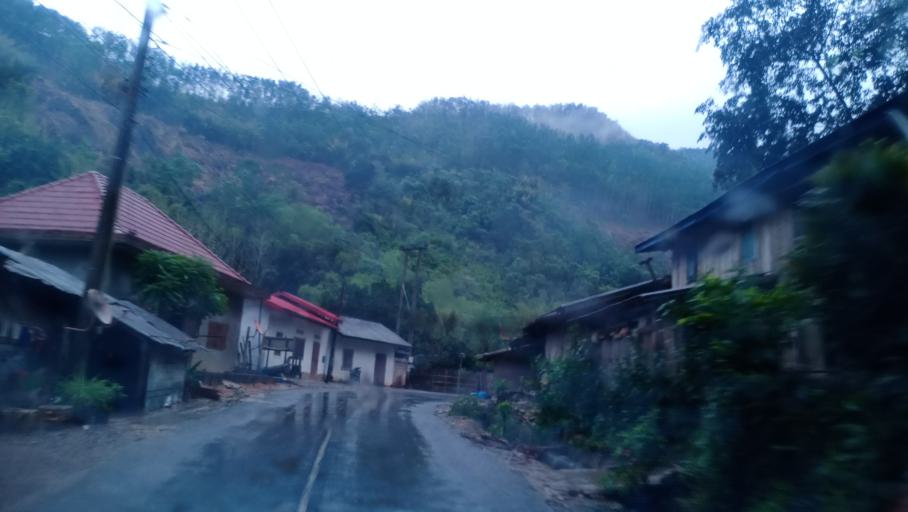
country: LA
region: Phongsali
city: Khoa
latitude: 21.0744
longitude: 102.5030
